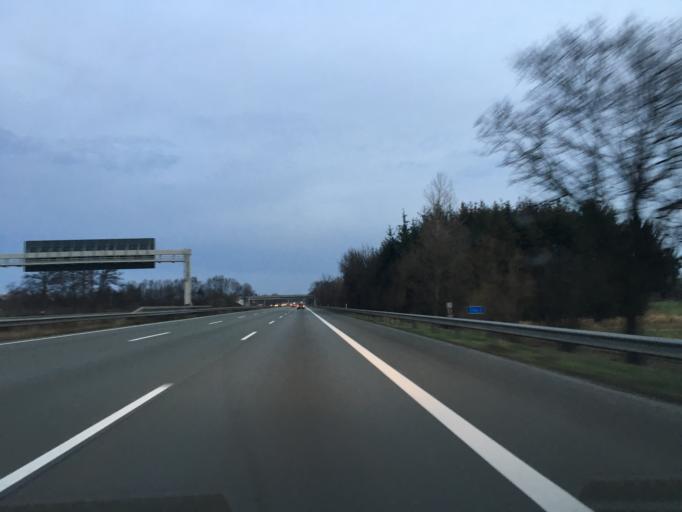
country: DE
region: Lower Saxony
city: Seevetal
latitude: 53.4066
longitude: 10.0282
